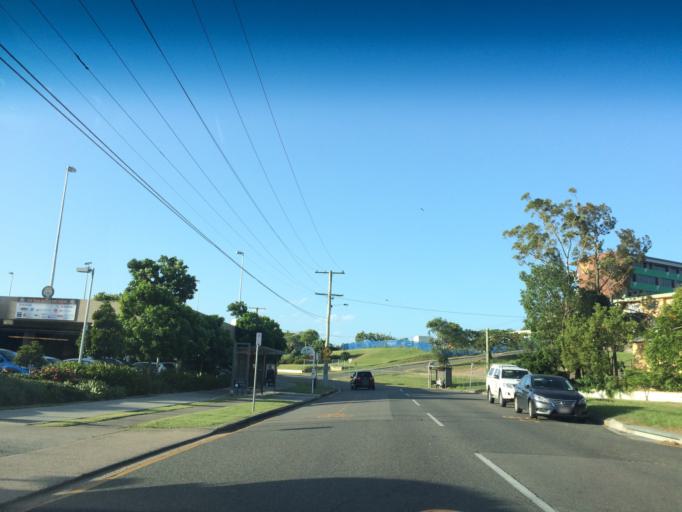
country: AU
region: Queensland
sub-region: Brisbane
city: Greenslopes
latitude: -27.4975
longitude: 153.0507
